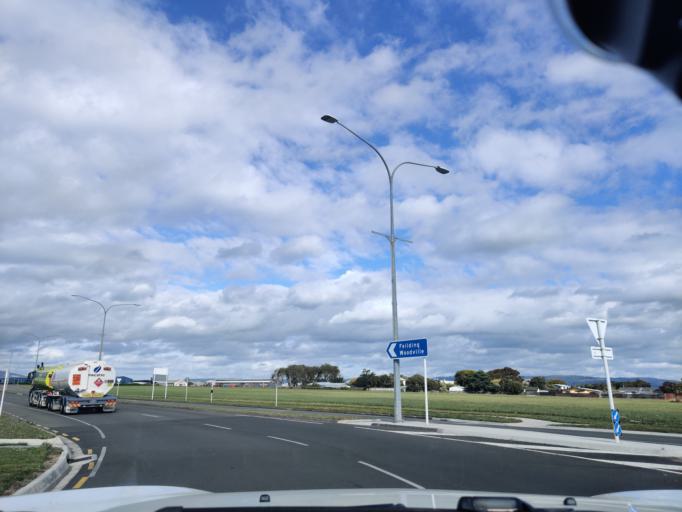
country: NZ
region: Manawatu-Wanganui
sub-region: Palmerston North City
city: Palmerston North
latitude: -40.3258
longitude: 175.6211
